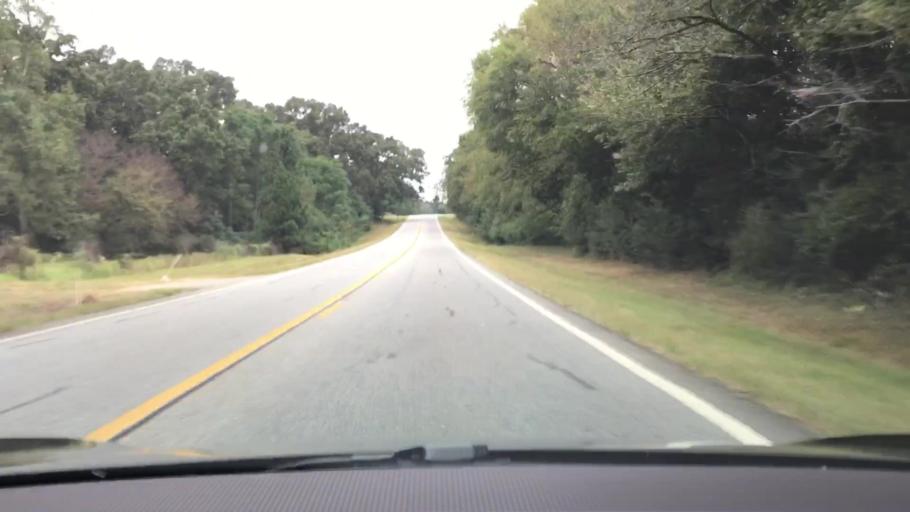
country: US
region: Georgia
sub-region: Oconee County
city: Watkinsville
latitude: 33.7724
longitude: -83.3104
